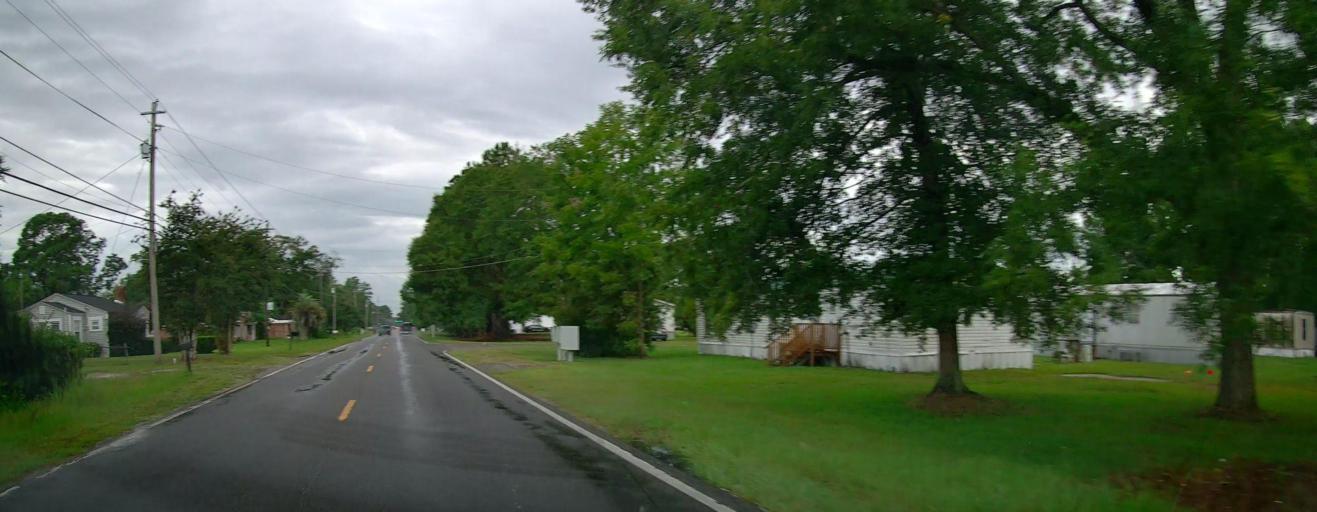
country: US
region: Georgia
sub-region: Ware County
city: Deenwood
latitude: 31.2139
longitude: -82.3838
